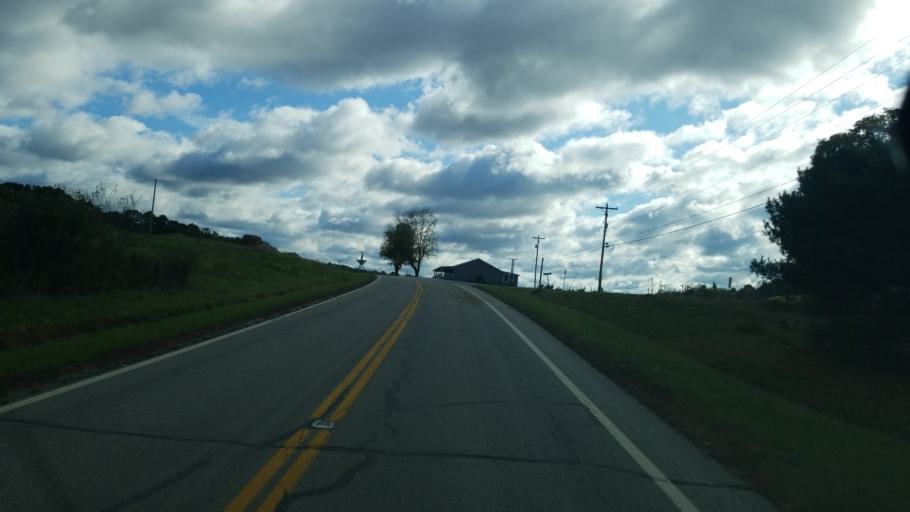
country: US
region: Ohio
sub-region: Jackson County
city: Wellston
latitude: 39.1597
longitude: -82.5100
